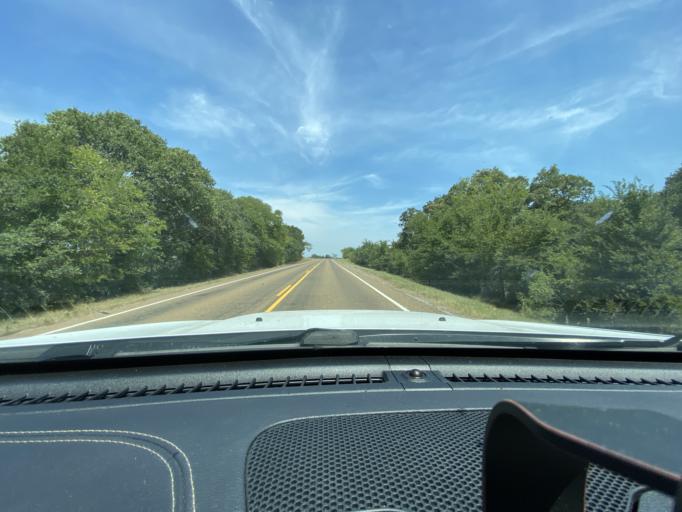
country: US
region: Texas
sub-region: Bastrop County
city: Smithville
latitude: 30.1119
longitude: -97.0804
